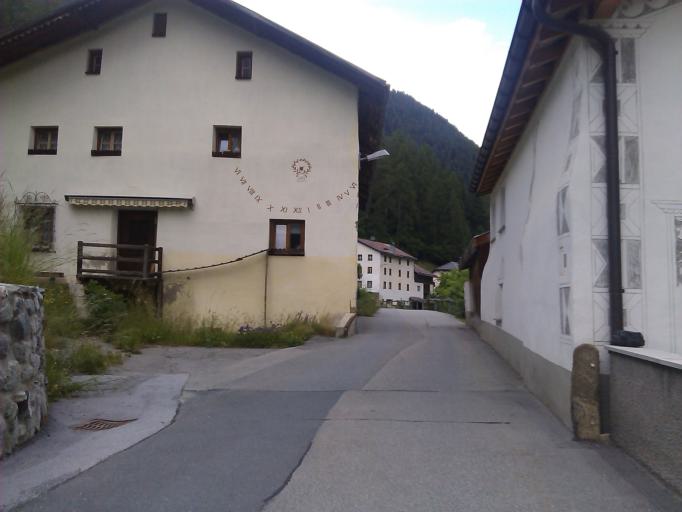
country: AT
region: Tyrol
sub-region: Politischer Bezirk Landeck
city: Nauders
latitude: 46.8815
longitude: 10.4593
